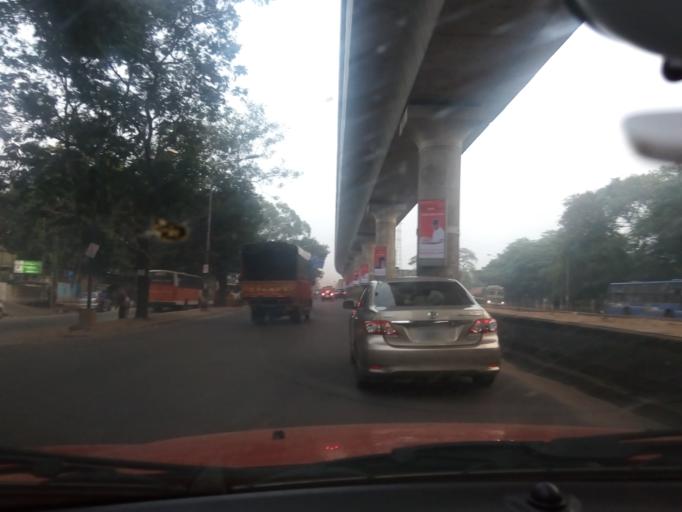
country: IN
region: Karnataka
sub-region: Bangalore Urban
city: Bangalore
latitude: 13.0289
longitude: 77.5400
